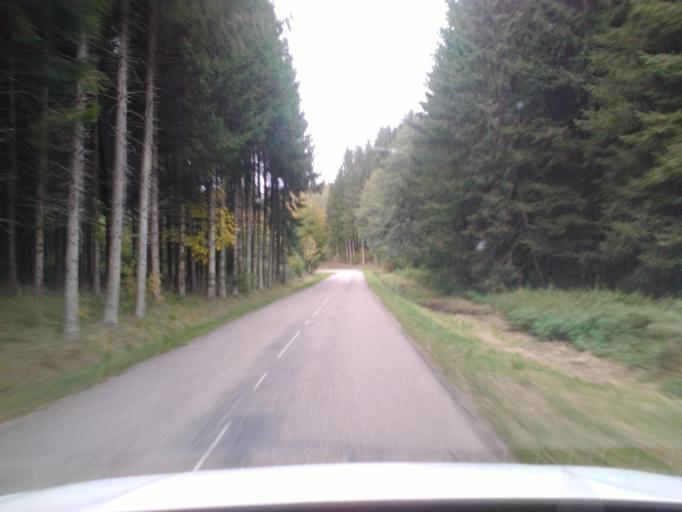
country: FR
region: Lorraine
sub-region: Departement des Vosges
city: Sainte-Marguerite
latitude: 48.3264
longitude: 7.0231
